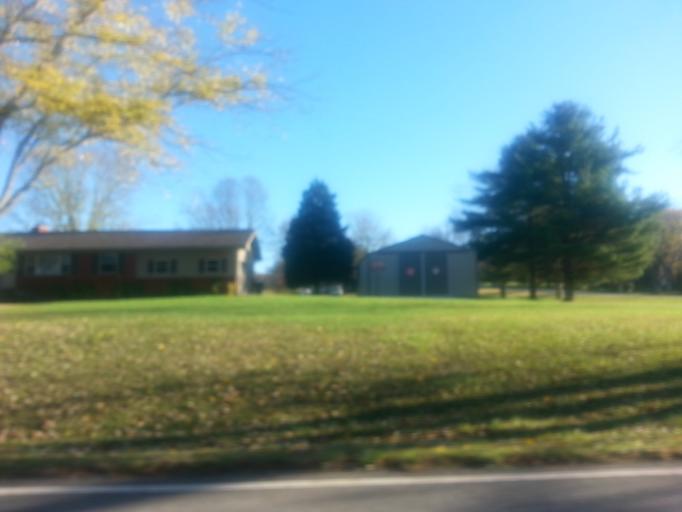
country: US
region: Tennessee
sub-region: Blount County
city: Eagleton Village
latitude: 35.8360
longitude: -83.9576
